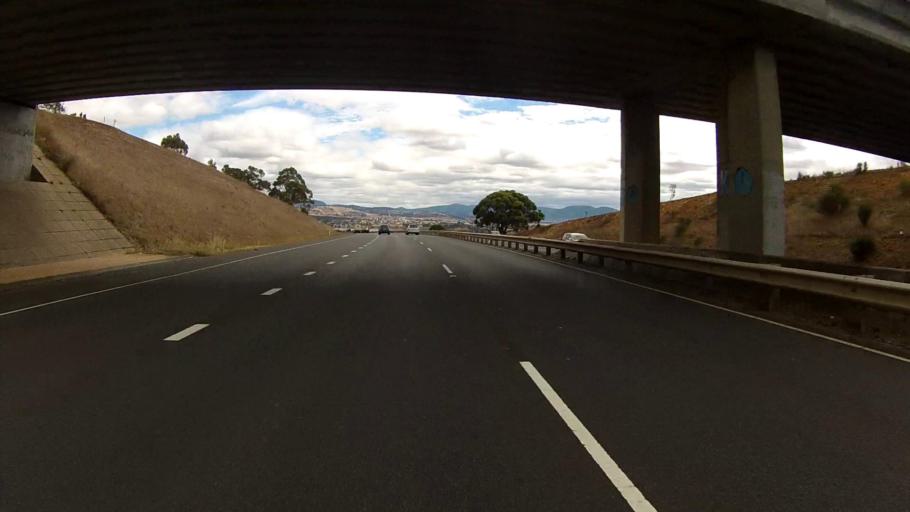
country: AU
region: Tasmania
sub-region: Glenorchy
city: Austins Ferry
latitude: -42.7743
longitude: 147.2389
